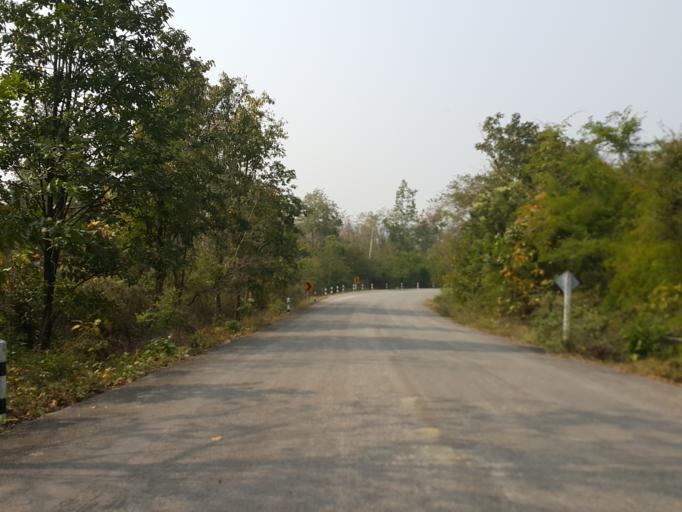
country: TH
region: Lampang
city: Mae Phrik
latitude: 17.4973
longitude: 99.0845
